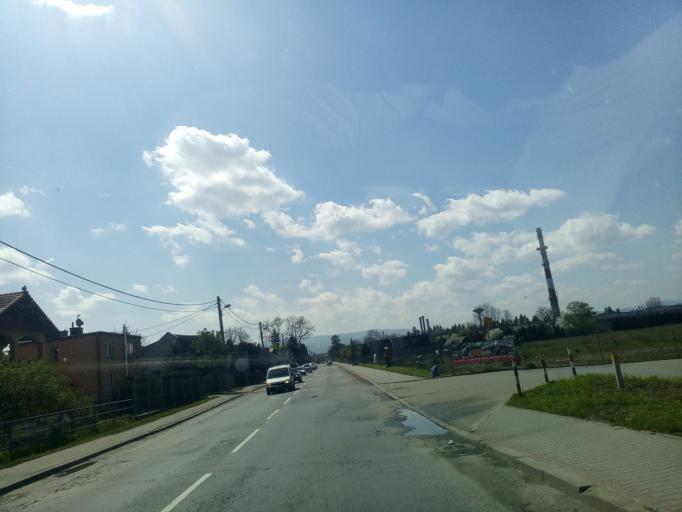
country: PL
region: Lesser Poland Voivodeship
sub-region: Powiat nowosadecki
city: Nowy Sacz
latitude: 49.5981
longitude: 20.6845
